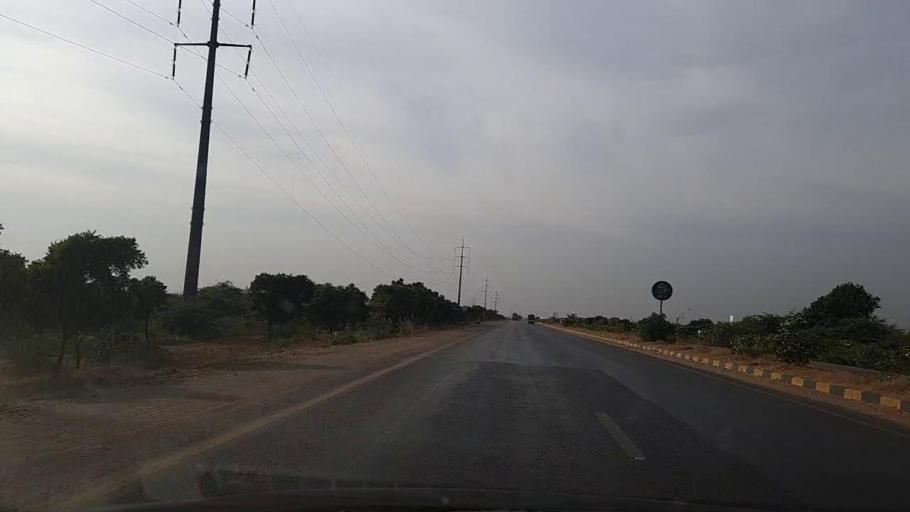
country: PK
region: Sindh
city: Gharo
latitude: 24.8329
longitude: 67.4600
